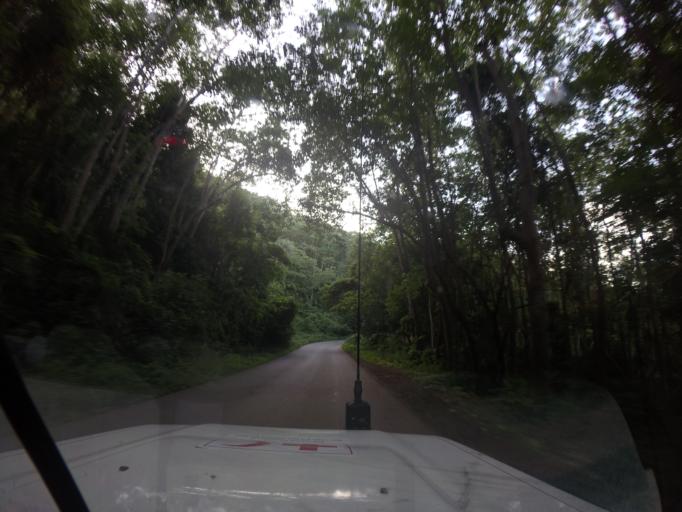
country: GN
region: Kindia
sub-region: Kindia
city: Kindia
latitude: 10.0121
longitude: -12.8107
